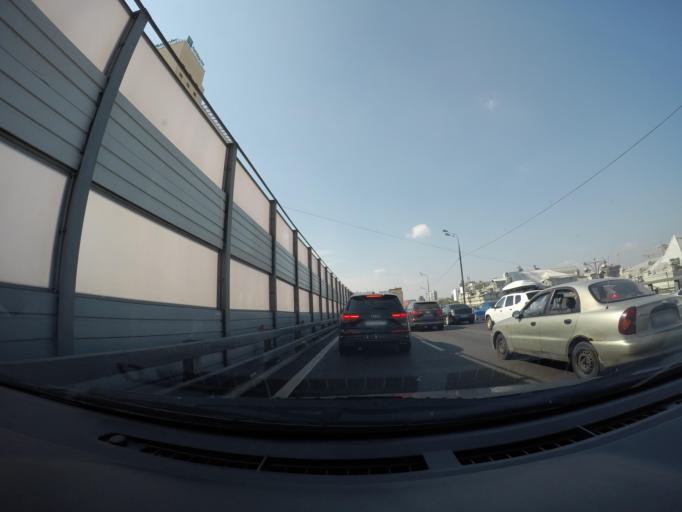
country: RU
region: Moscow
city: Mar'ina Roshcha
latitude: 55.7919
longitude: 37.6336
